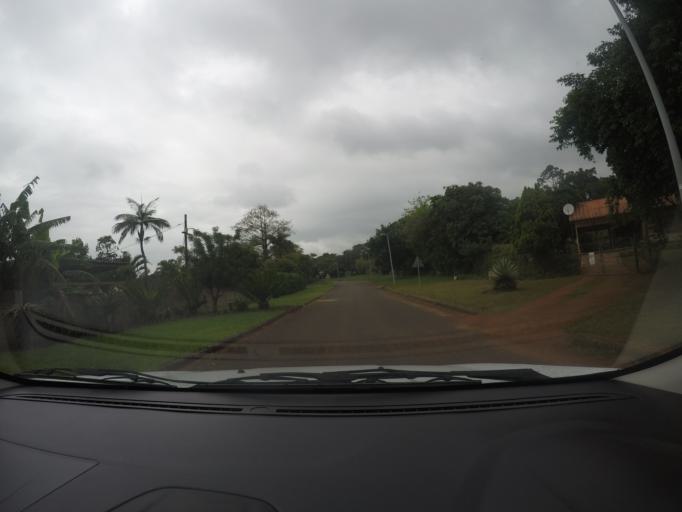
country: ZA
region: KwaZulu-Natal
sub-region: uThungulu District Municipality
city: Empangeni
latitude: -28.7595
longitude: 31.8959
